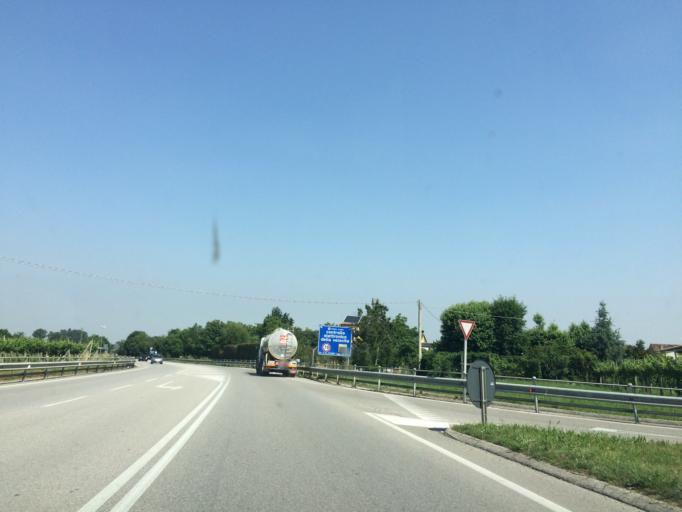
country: IT
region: Veneto
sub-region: Provincia di Padova
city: Cittadella
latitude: 45.6273
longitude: 11.7918
